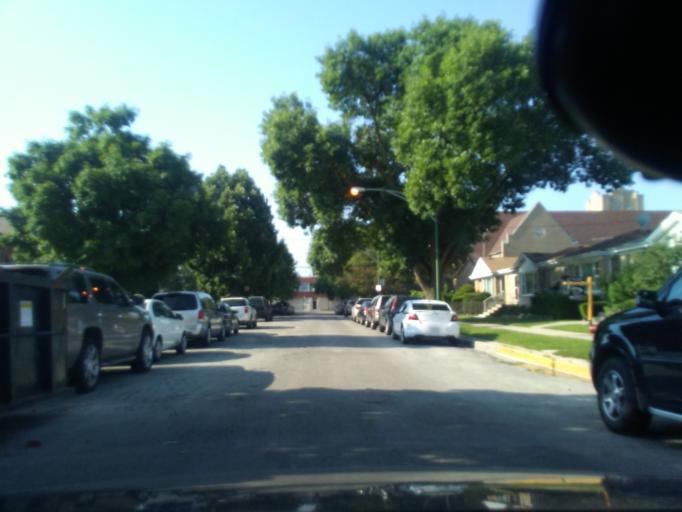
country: US
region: Illinois
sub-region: Cook County
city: Elmwood Park
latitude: 41.9324
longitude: -87.7626
